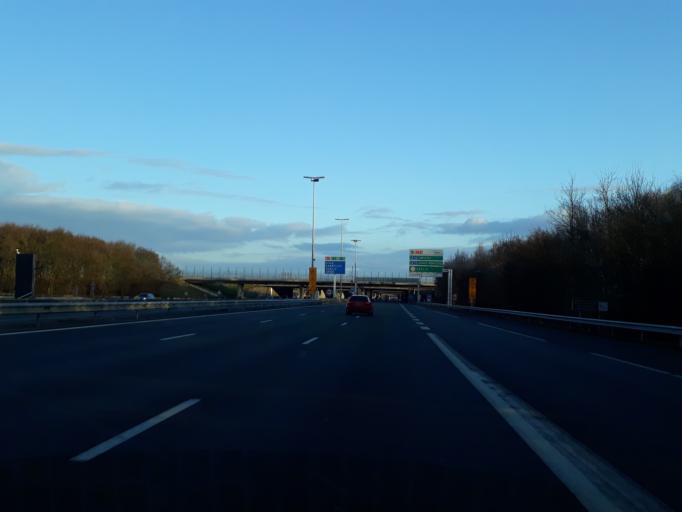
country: FR
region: Ile-de-France
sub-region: Departement du Val-d'Oise
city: Roissy-en-France
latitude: 49.0140
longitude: 2.5308
